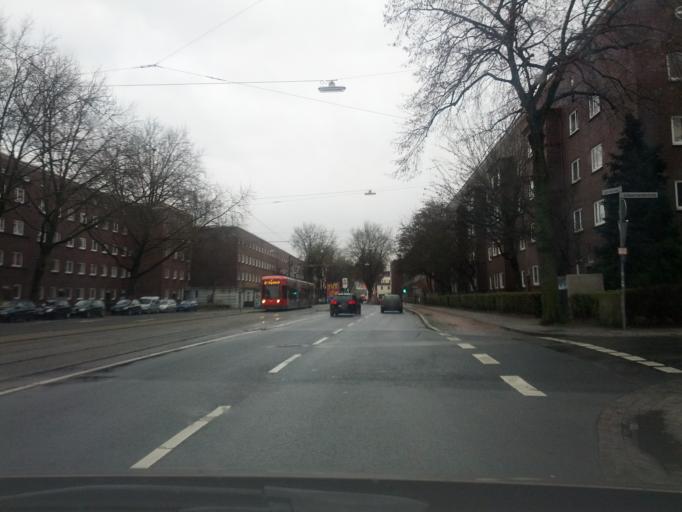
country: DE
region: Bremen
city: Bremen
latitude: 53.0632
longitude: 8.7886
